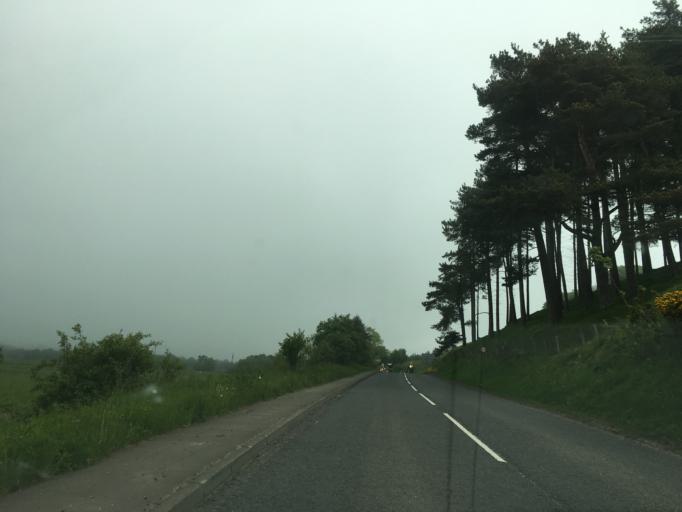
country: GB
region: Scotland
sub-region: The Scottish Borders
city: West Linton
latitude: 55.7195
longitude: -3.3367
